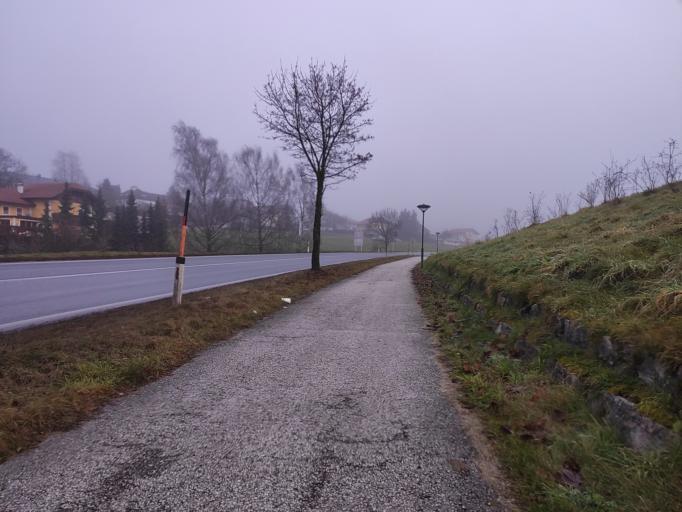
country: AT
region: Salzburg
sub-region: Politischer Bezirk Salzburg-Umgebung
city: Strasswalchen
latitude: 47.9821
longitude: 13.2595
